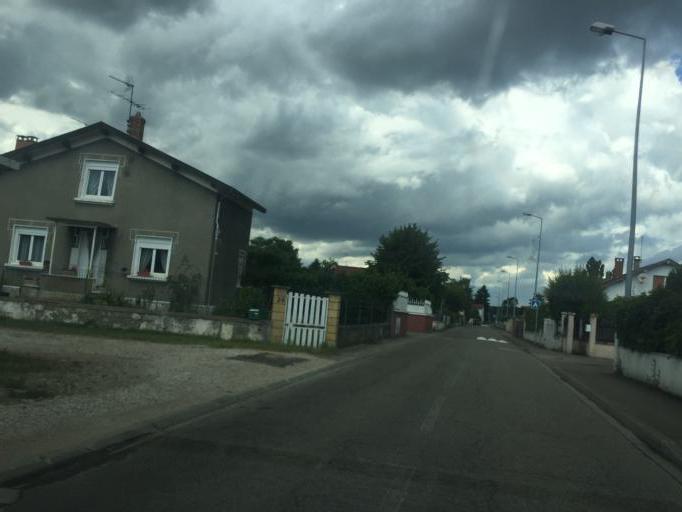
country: FR
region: Rhone-Alpes
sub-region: Departement de l'Isere
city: Pont-de-Cheruy
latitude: 45.7543
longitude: 5.1682
